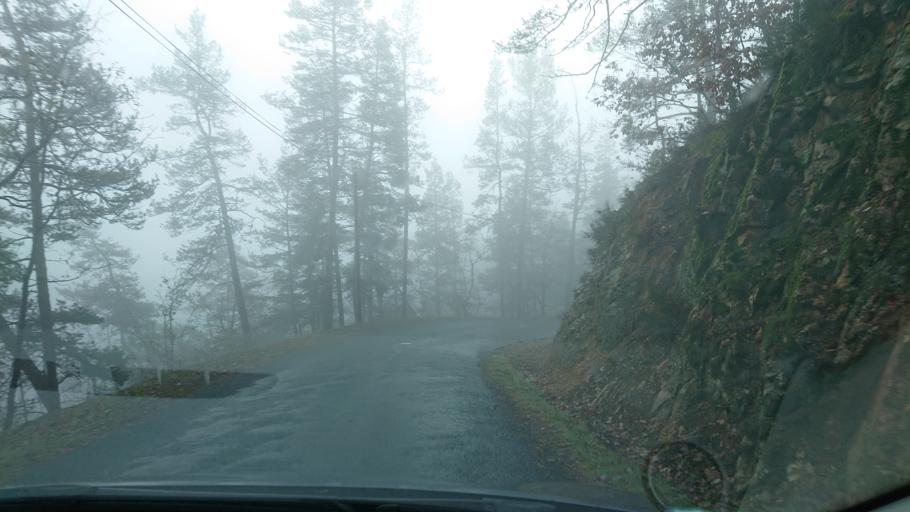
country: FR
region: Auvergne
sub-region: Departement de la Haute-Loire
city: Vorey
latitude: 45.2043
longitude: 3.9196
